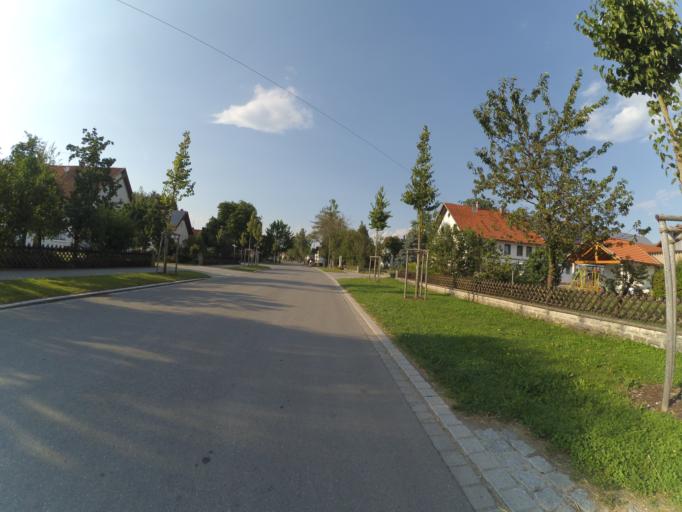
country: DE
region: Bavaria
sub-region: Swabia
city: Bad Worishofen
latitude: 48.0556
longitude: 10.5874
